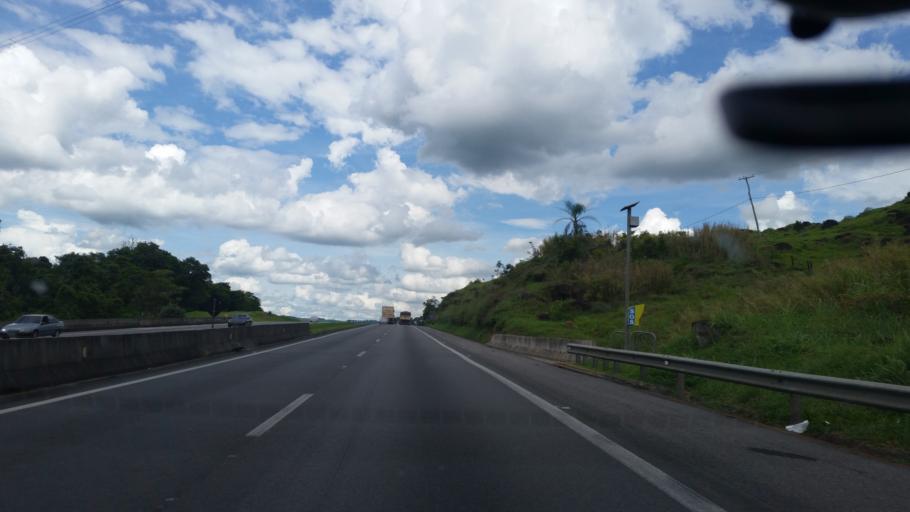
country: BR
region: Sao Paulo
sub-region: Itatiba
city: Itatiba
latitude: -22.9357
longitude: -46.8940
